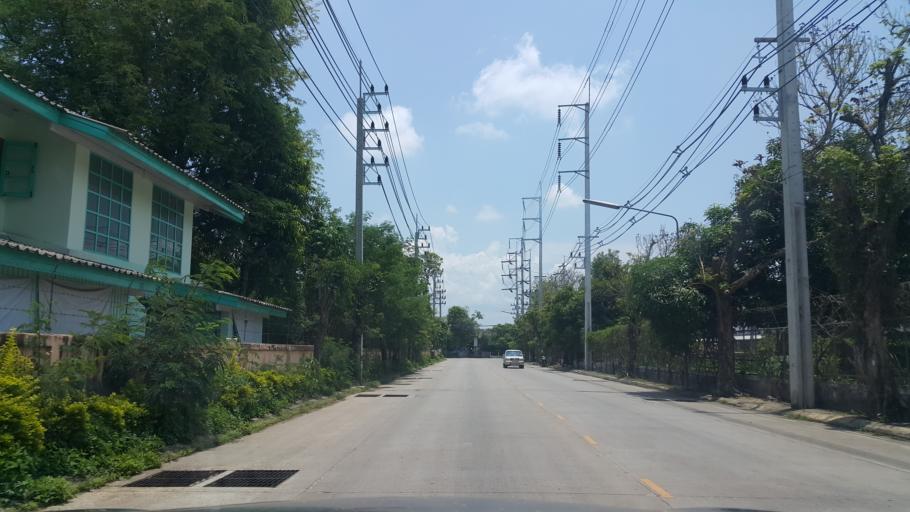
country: TH
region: Chiang Rai
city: Chiang Rai
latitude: 19.9097
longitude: 99.8219
